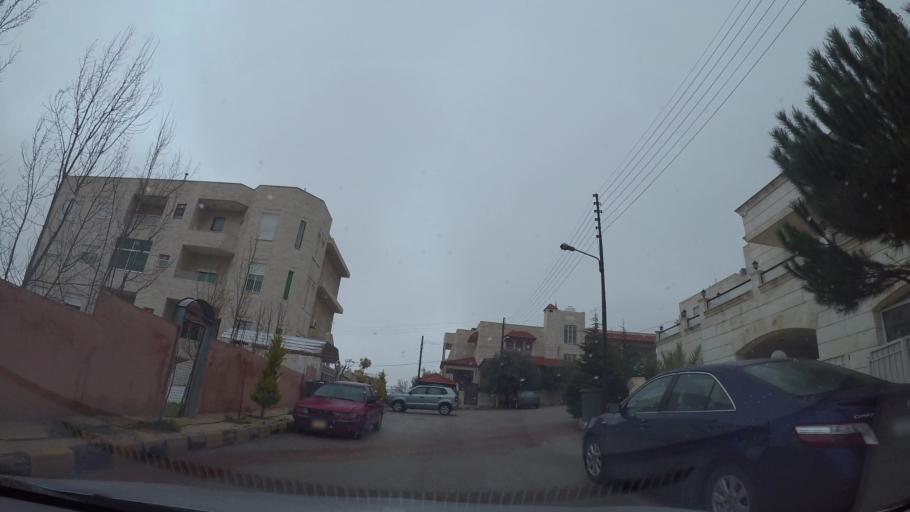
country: JO
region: Amman
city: Al Jubayhah
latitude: 32.0355
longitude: 35.8542
